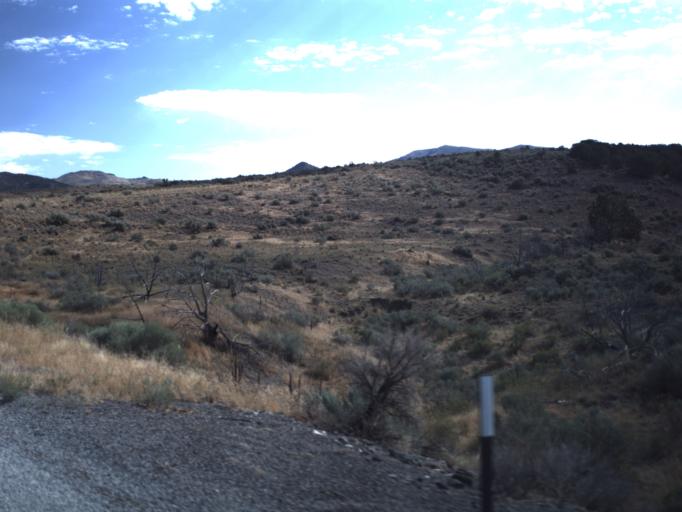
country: US
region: Utah
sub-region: Juab County
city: Mona
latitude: 39.7825
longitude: -112.1516
